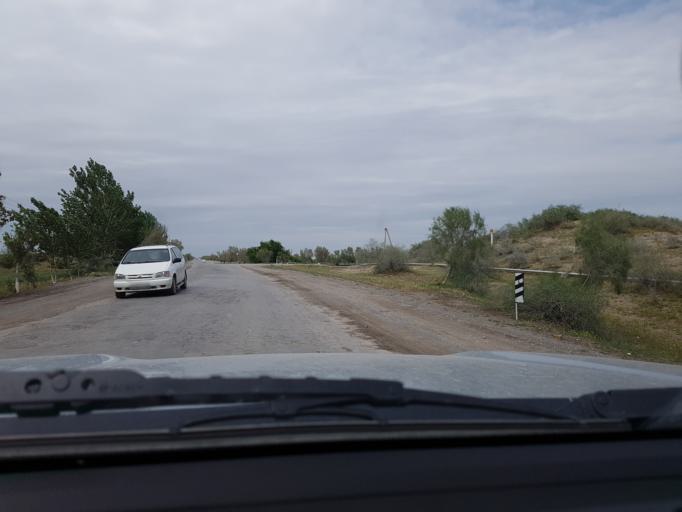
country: TM
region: Lebap
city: Atamyrat
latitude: 38.1130
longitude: 64.7344
